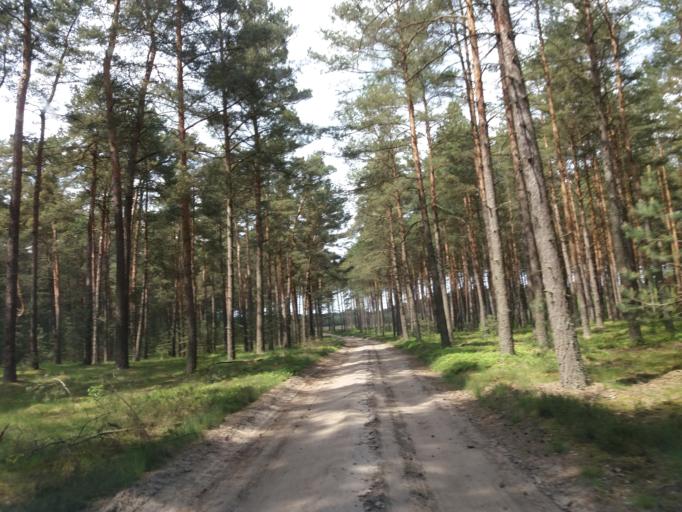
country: PL
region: West Pomeranian Voivodeship
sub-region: Powiat choszczenski
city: Drawno
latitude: 53.1584
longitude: 15.7570
